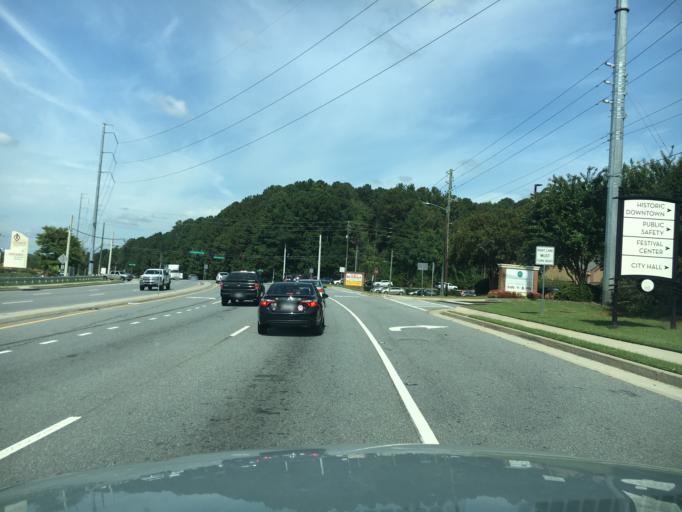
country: US
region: Georgia
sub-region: Gwinnett County
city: Duluth
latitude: 34.0013
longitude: -84.1619
